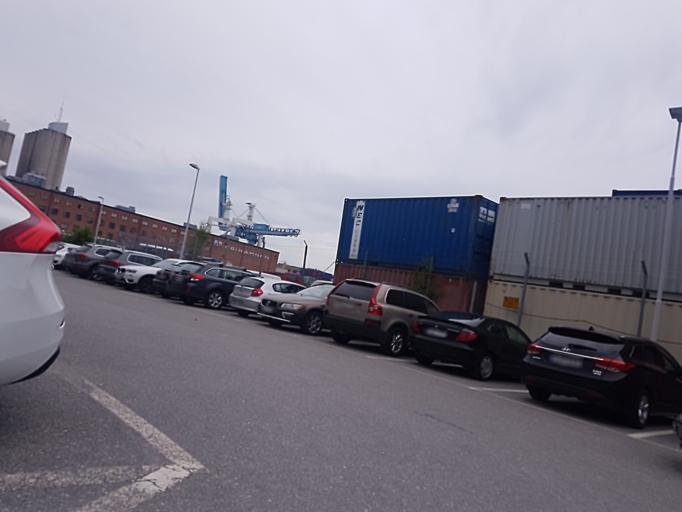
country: SE
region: Stockholm
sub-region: Lidingo
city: Lidingoe
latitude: 59.3397
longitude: 18.1234
